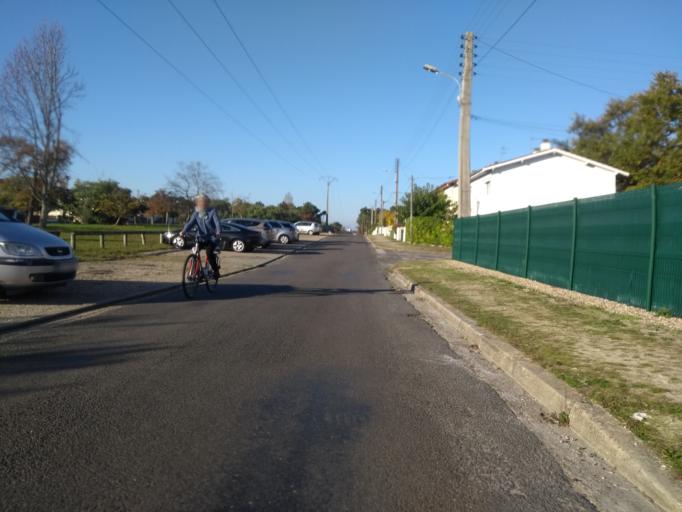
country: FR
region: Aquitaine
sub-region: Departement de la Gironde
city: Gradignan
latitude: 44.7675
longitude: -0.5862
